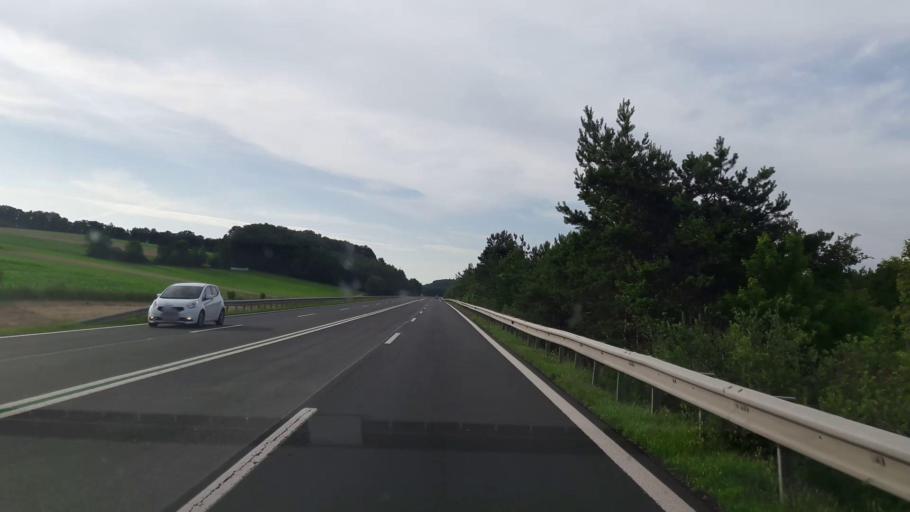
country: AT
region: Burgenland
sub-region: Politischer Bezirk Oberpullendorf
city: Kobersdorf
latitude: 47.6235
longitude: 16.3869
